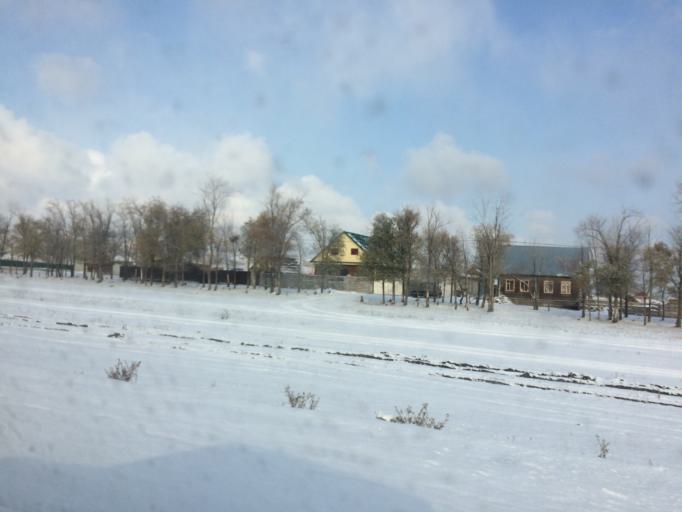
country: RU
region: Chelyabinsk
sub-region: Gorod Magnitogorsk
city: Magnitogorsk
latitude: 53.3529
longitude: 58.6510
